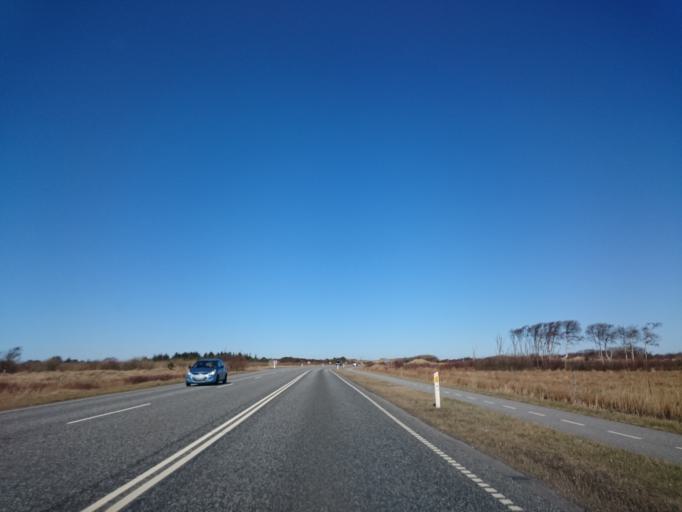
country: DK
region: North Denmark
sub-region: Frederikshavn Kommune
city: Skagen
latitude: 57.6691
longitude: 10.4544
